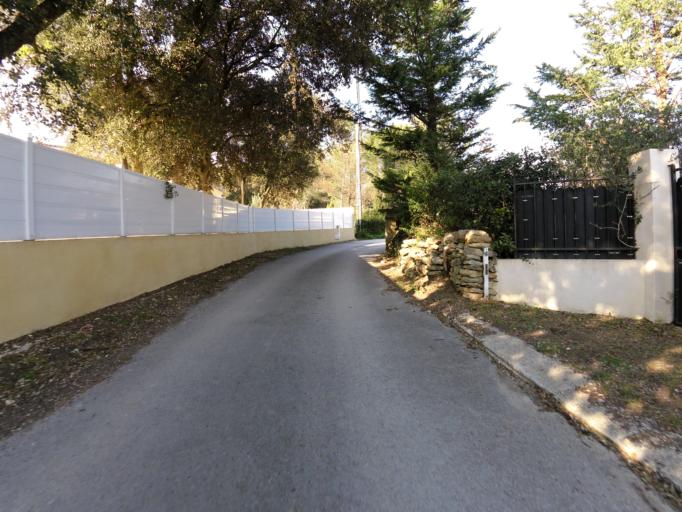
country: FR
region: Languedoc-Roussillon
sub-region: Departement du Gard
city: Aigues-Vives
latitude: 43.7424
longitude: 4.1655
